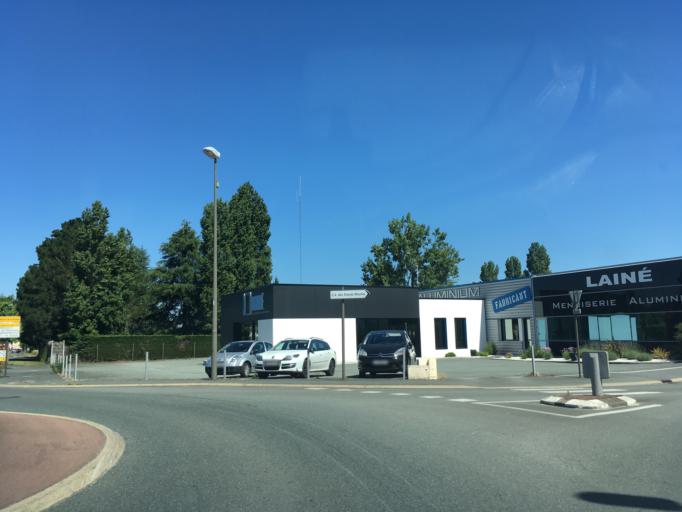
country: FR
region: Pays de la Loire
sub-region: Departement de la Vendee
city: Saint-Georges-de-Montaigu
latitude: 46.9430
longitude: -1.2871
